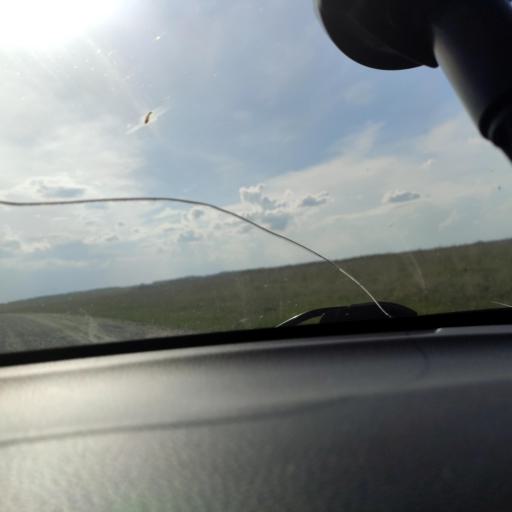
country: RU
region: Tatarstan
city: Verkhniy Uslon
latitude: 55.6470
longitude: 48.9286
